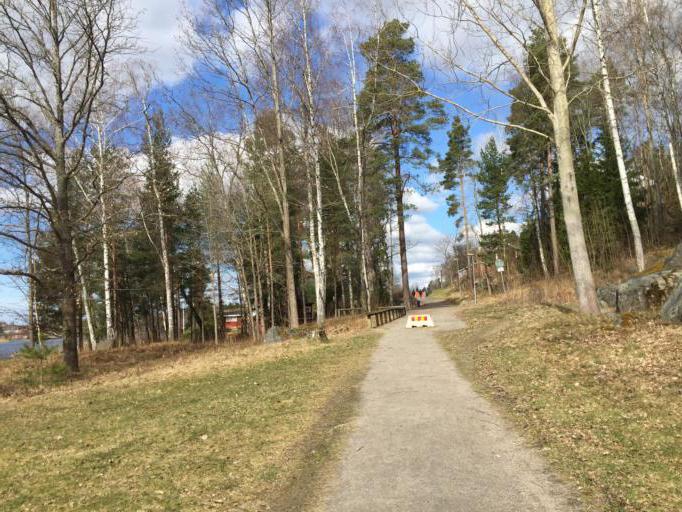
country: SE
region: Soedermanland
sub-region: Katrineholms Kommun
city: Katrineholm
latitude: 58.9836
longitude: 16.1732
